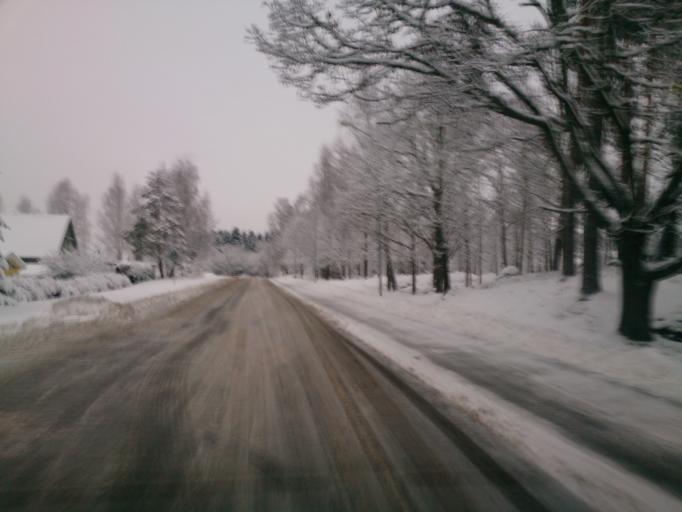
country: SE
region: OEstergoetland
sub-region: Atvidabergs Kommun
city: Atvidaberg
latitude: 58.1994
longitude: 15.9848
